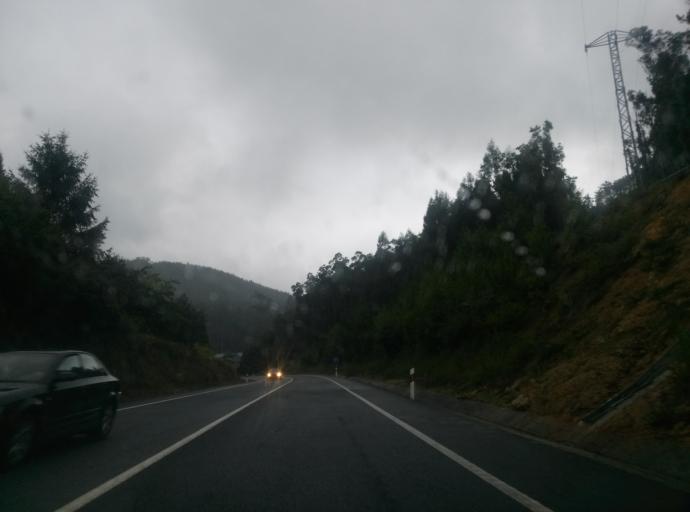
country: ES
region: Galicia
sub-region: Provincia de Lugo
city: Viveiro
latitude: 43.5917
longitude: -7.6229
